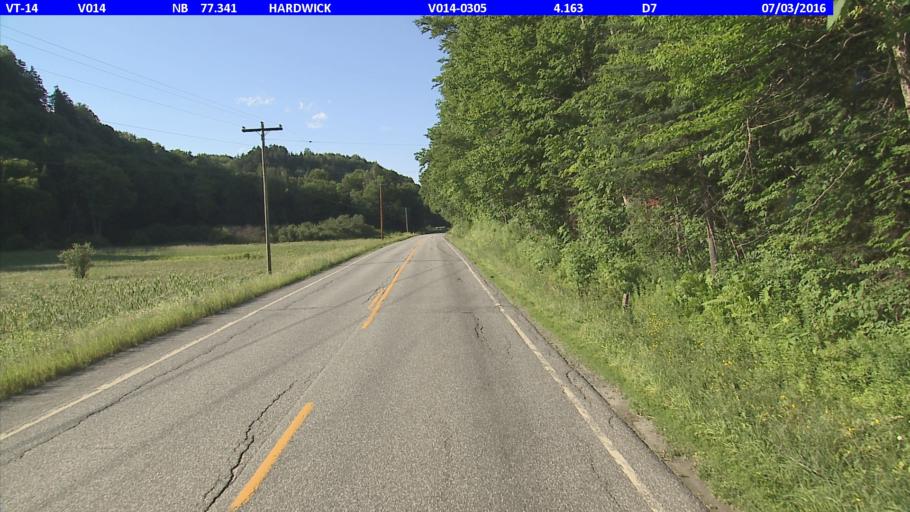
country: US
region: Vermont
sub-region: Caledonia County
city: Hardwick
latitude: 44.5535
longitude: -72.3693
